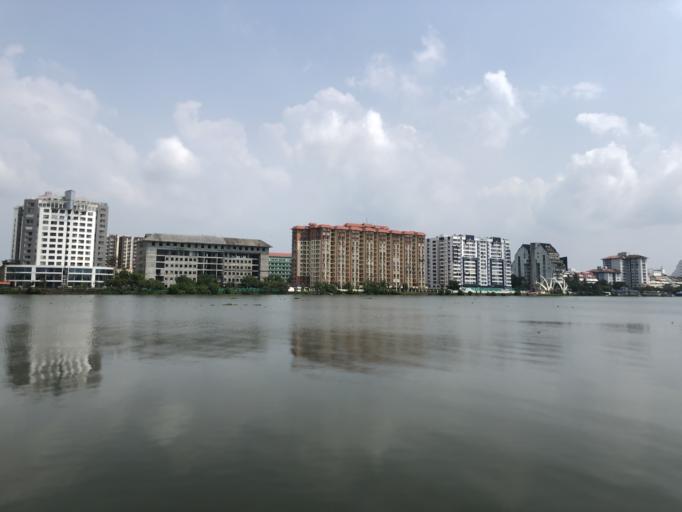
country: IN
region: Kerala
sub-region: Ernakulam
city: Cochin
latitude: 9.9884
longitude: 76.2675
